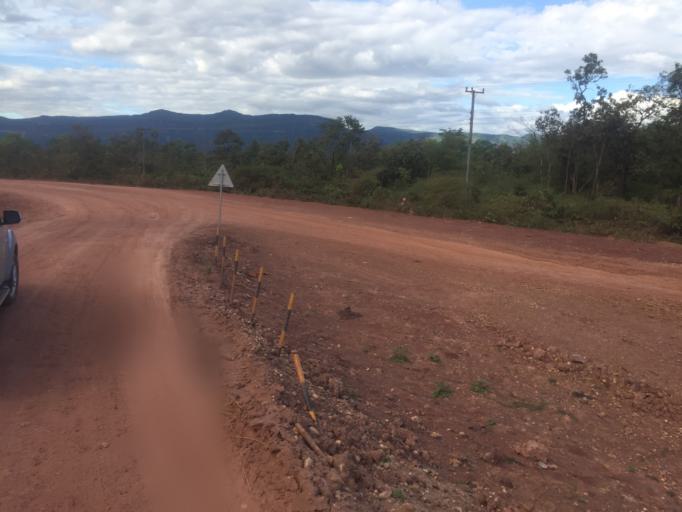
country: LA
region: Attapu
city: Attapu
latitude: 14.6920
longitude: 106.5365
